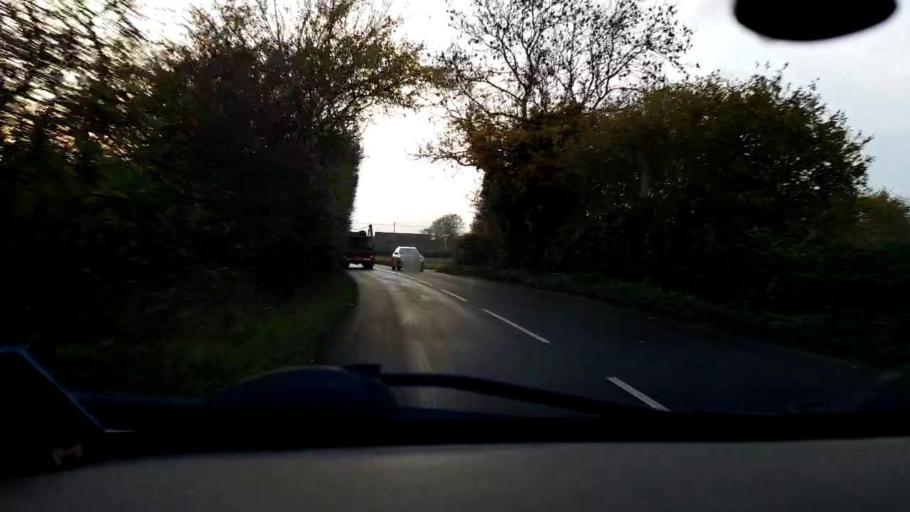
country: GB
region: England
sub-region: Norfolk
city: Mattishall
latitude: 52.6969
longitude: 1.0929
